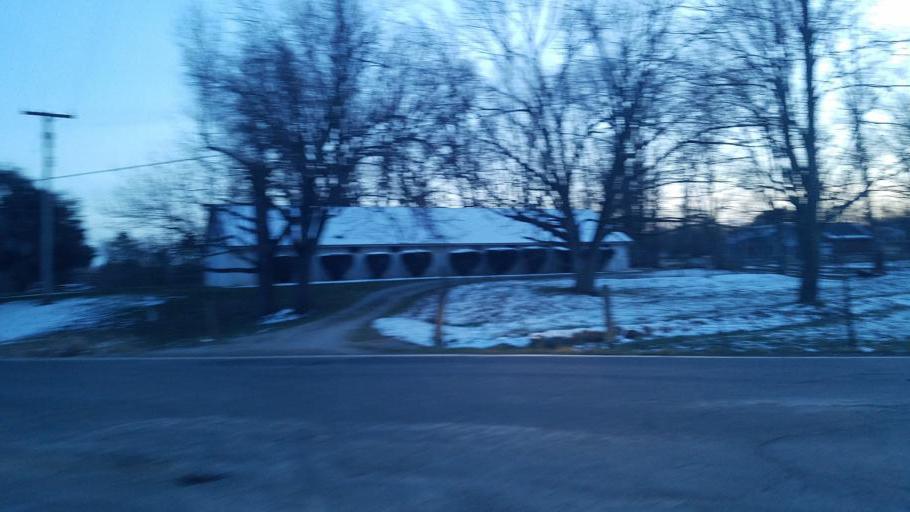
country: US
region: Ohio
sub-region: Ashland County
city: Ashland
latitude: 40.8334
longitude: -82.2797
